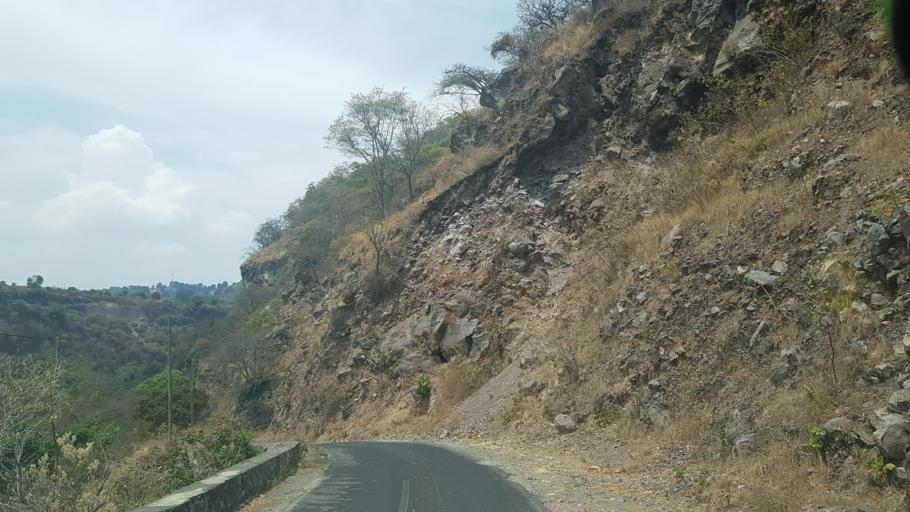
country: MX
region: Puebla
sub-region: Tochimilco
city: La Magdalena Yancuitlalpan
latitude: 18.8741
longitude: -98.6034
